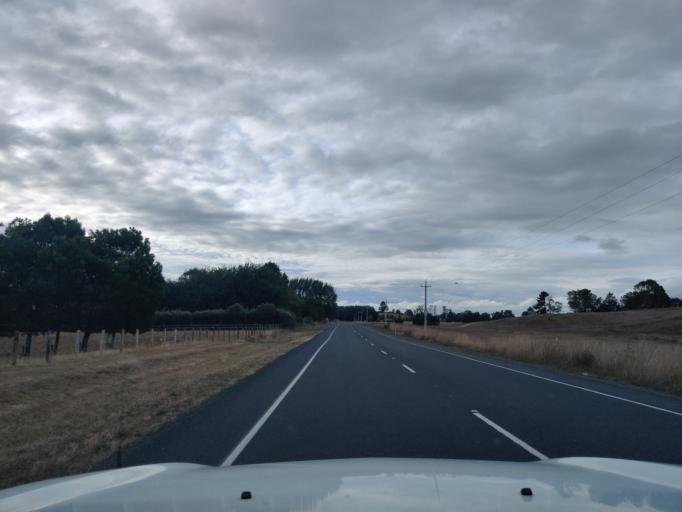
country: NZ
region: Waikato
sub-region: Waipa District
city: Cambridge
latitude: -37.8119
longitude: 175.4532
